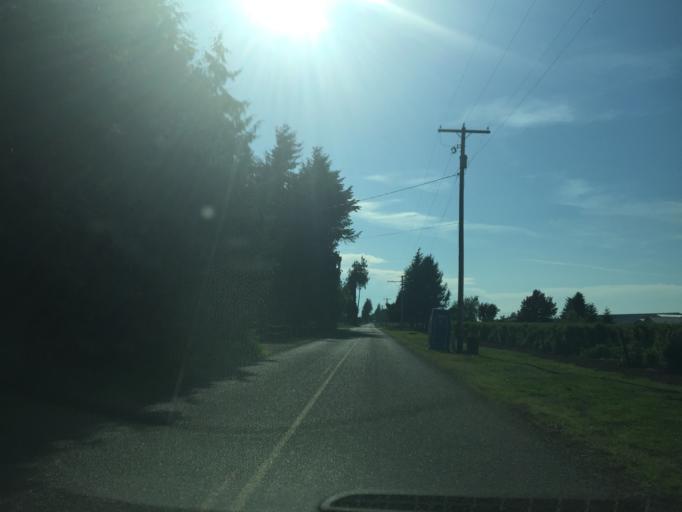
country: US
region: Washington
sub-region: Whatcom County
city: Lynden
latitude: 48.9969
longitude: -122.4500
